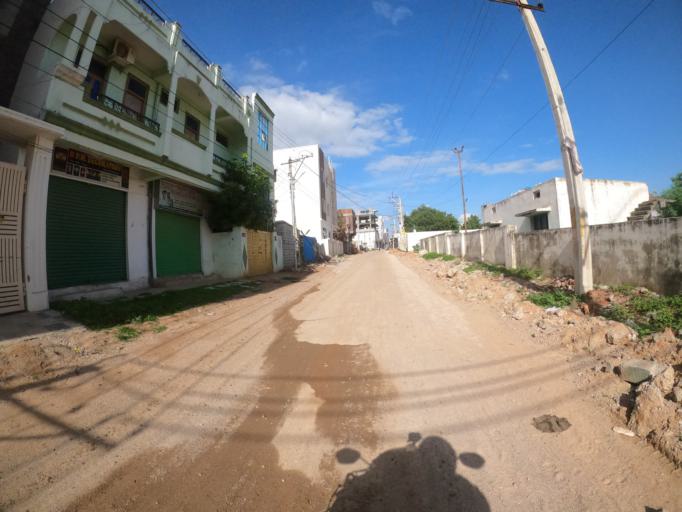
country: IN
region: Telangana
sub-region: Hyderabad
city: Hyderabad
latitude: 17.3602
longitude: 78.3771
